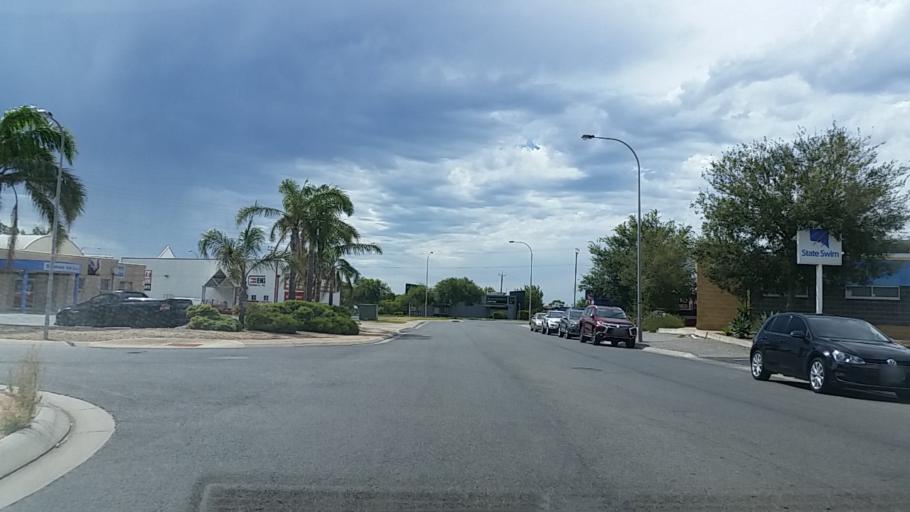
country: AU
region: South Australia
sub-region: Onkaparinga
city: Moana
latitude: -35.1924
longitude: 138.4789
